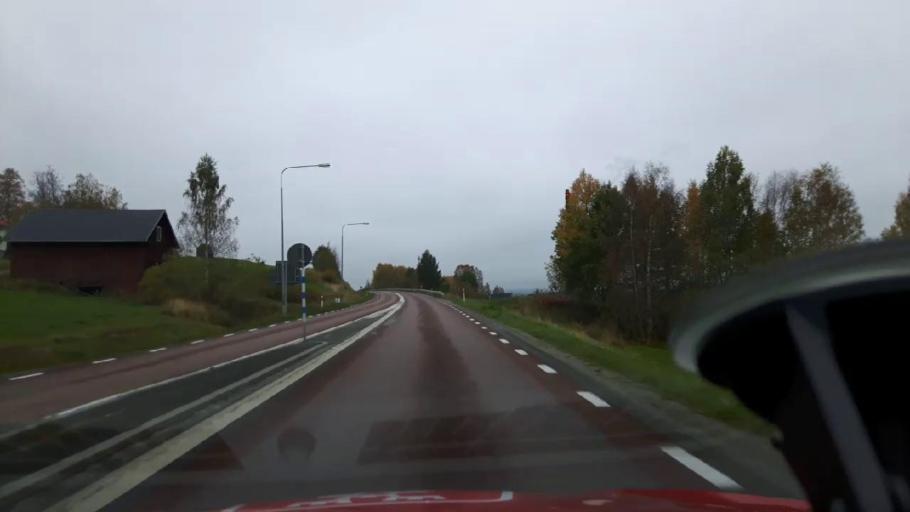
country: SE
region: Jaemtland
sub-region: Bergs Kommun
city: Hoverberg
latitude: 62.7666
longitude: 14.4390
